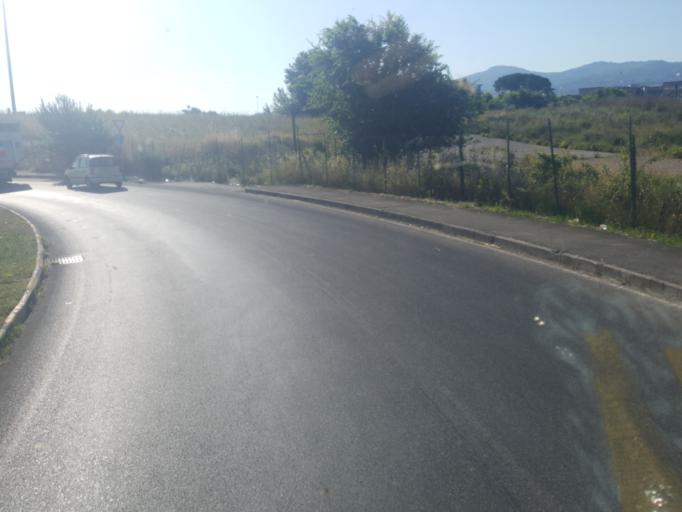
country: IT
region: Latium
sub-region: Citta metropolitana di Roma Capitale
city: Frascati
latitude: 41.8417
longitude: 12.6419
